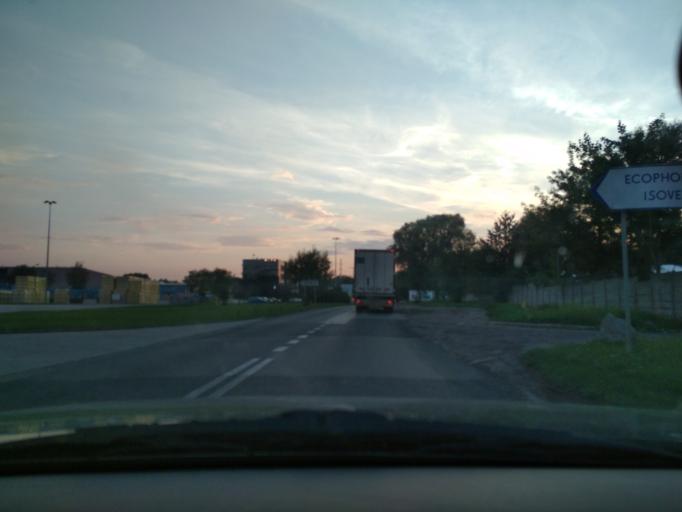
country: PL
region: Silesian Voivodeship
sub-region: Powiat gliwicki
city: Przyszowice
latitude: 50.2664
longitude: 18.7085
